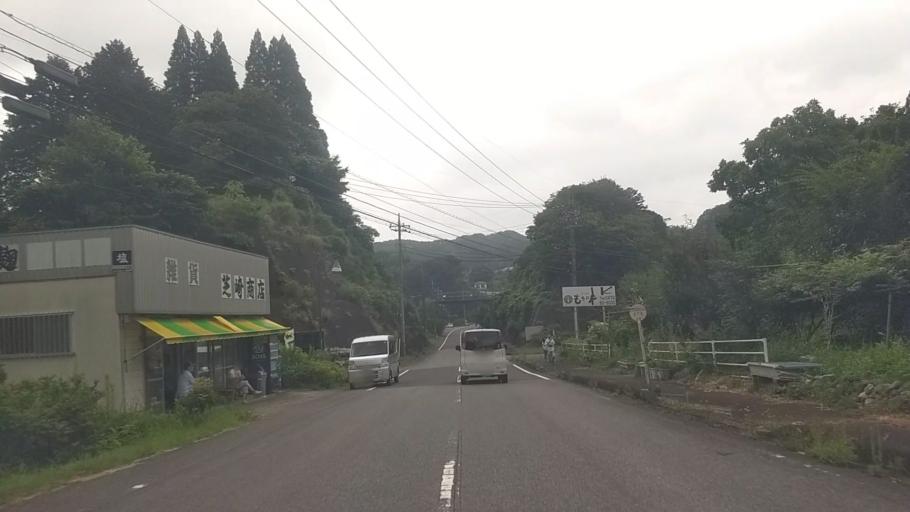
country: JP
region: Chiba
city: Kawaguchi
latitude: 35.2389
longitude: 140.1665
